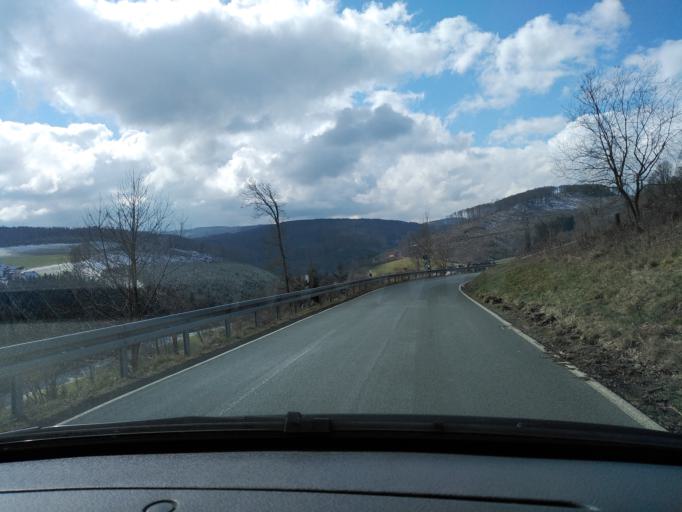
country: DE
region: North Rhine-Westphalia
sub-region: Regierungsbezirk Arnsberg
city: Brilon
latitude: 51.3787
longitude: 8.6339
